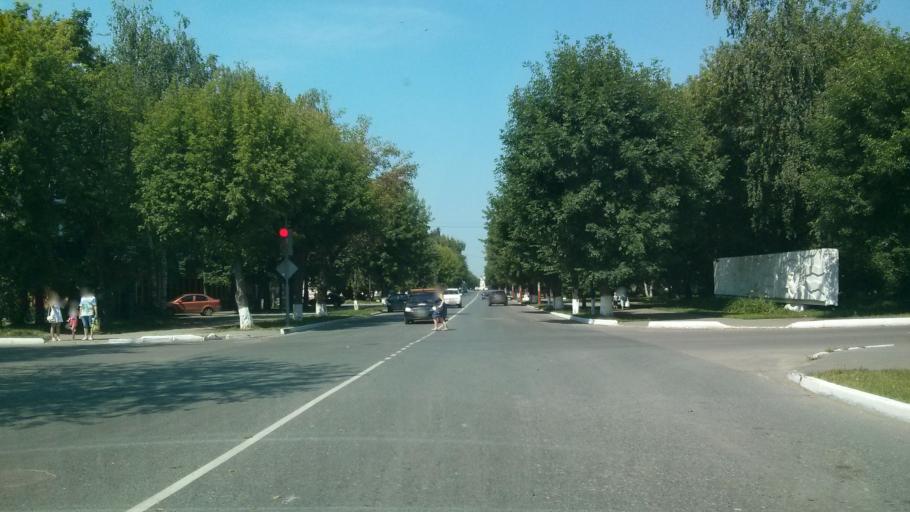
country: RU
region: Vladimir
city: Murom
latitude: 55.5693
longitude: 42.0548
